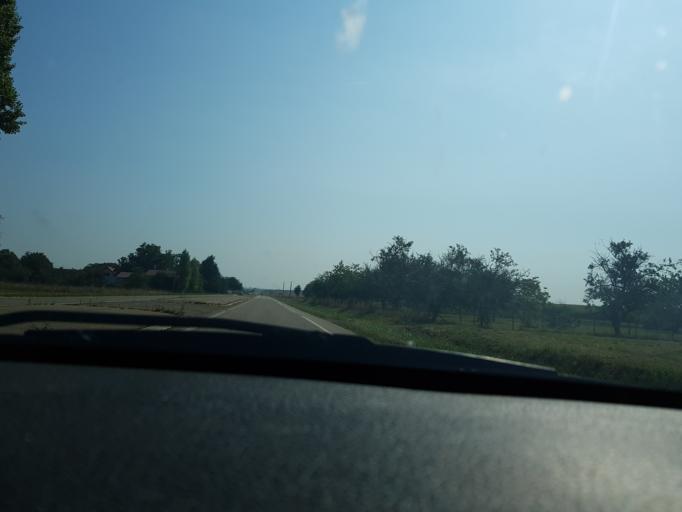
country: FR
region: Lorraine
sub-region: Departement de Meurthe-et-Moselle
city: Pont-a-Mousson
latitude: 48.9441
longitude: 6.1380
